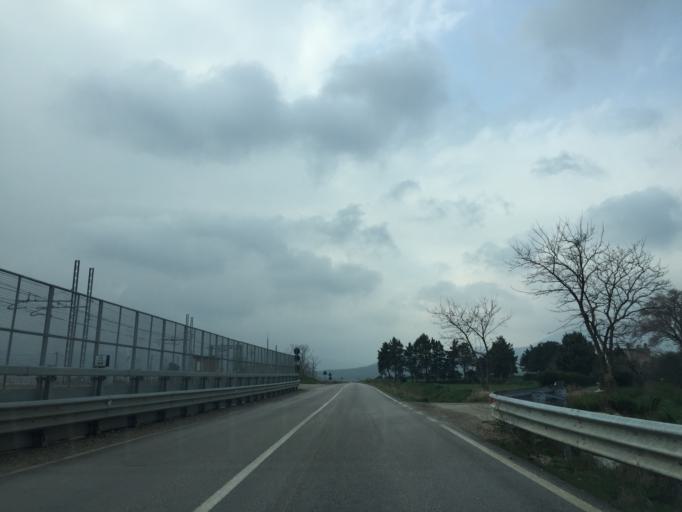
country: IT
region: Apulia
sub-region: Provincia di Foggia
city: Bovino
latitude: 41.3010
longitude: 15.3943
